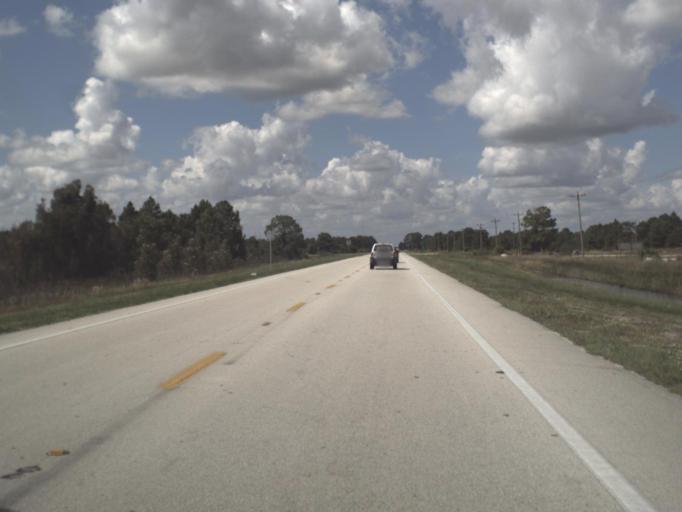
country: US
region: Florida
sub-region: Lee County
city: Lehigh Acres
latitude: 26.5180
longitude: -81.5618
